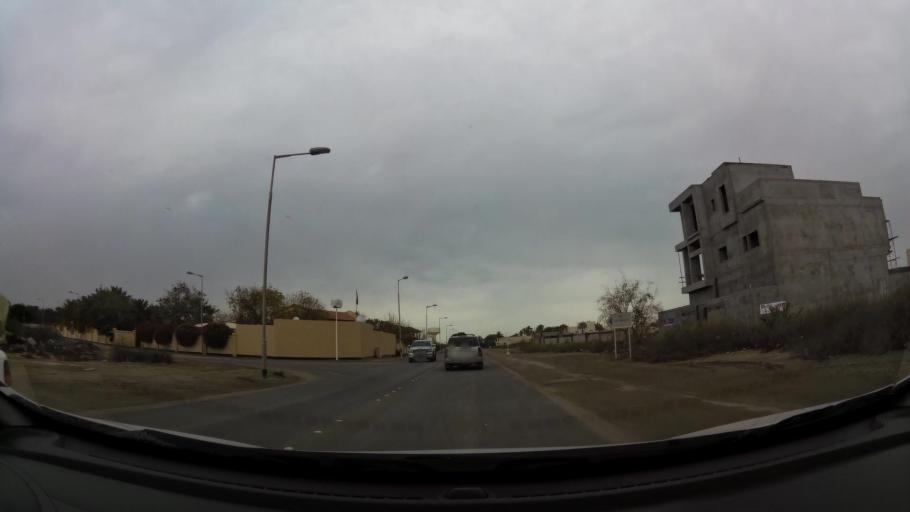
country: BH
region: Central Governorate
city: Madinat Hamad
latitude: 26.1350
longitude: 50.4648
